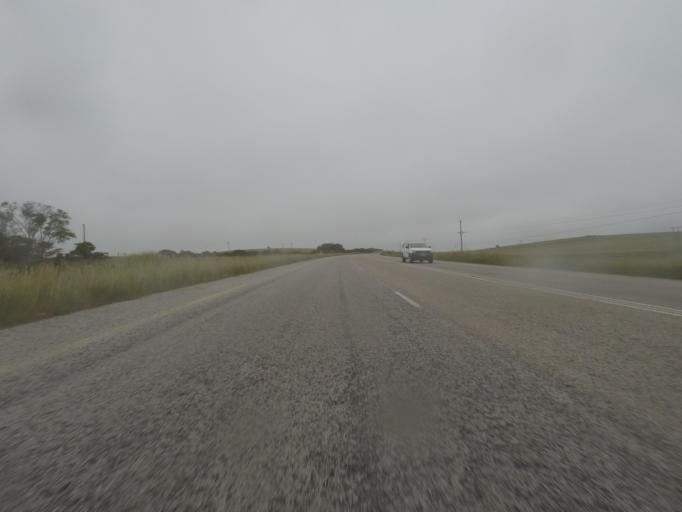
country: ZA
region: Eastern Cape
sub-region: Cacadu District Municipality
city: Grahamstown
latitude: -33.6235
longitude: 26.2921
